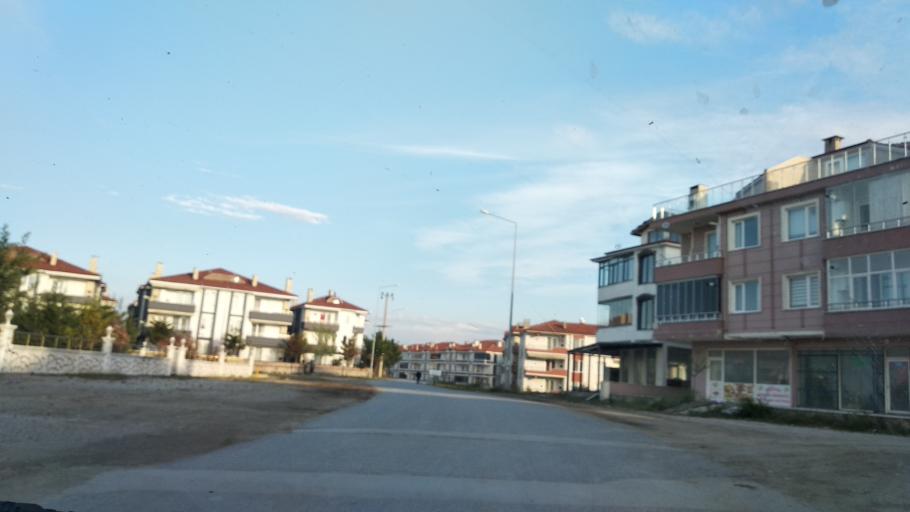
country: TR
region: Sakarya
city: Karasu
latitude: 41.0969
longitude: 30.7228
